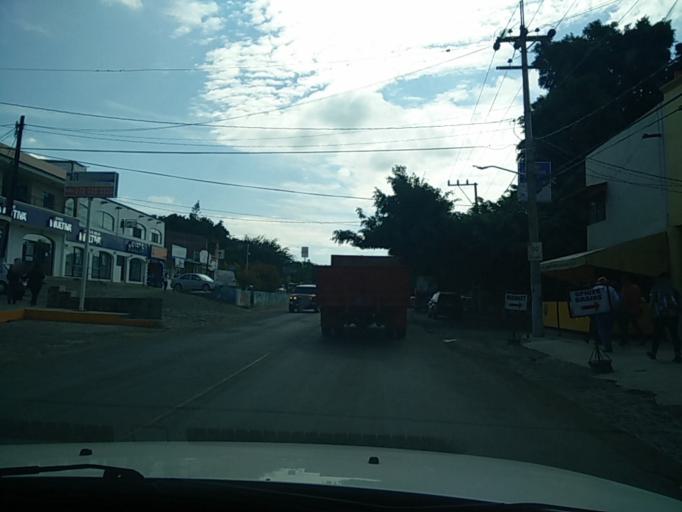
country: MX
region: Jalisco
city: Ajijic
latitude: 20.3009
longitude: -103.2597
